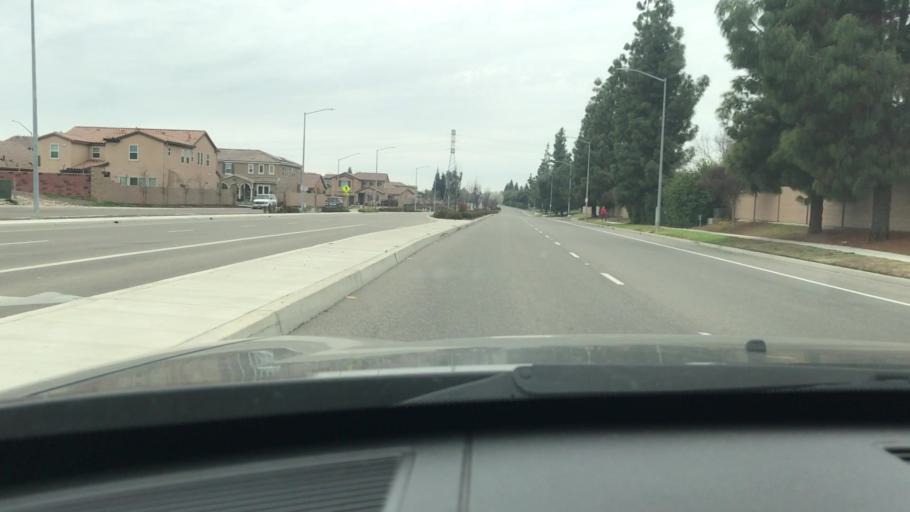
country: US
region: California
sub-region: Fresno County
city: Clovis
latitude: 36.8297
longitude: -119.6639
